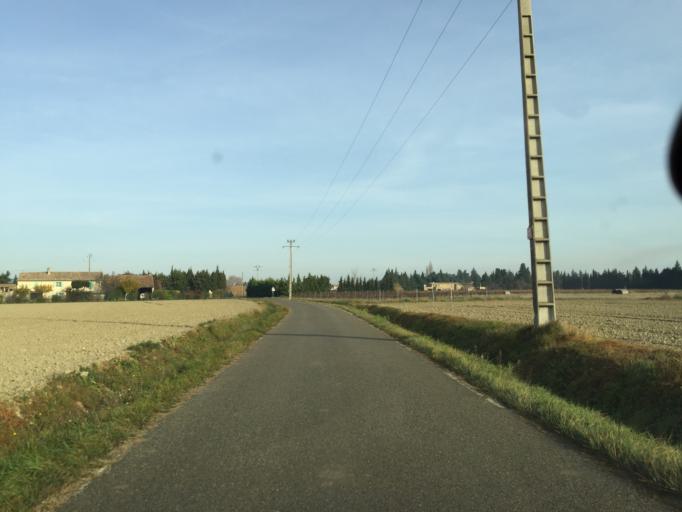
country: FR
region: Provence-Alpes-Cote d'Azur
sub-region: Departement du Vaucluse
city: Serignan-du-Comtat
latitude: 44.1652
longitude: 4.8391
